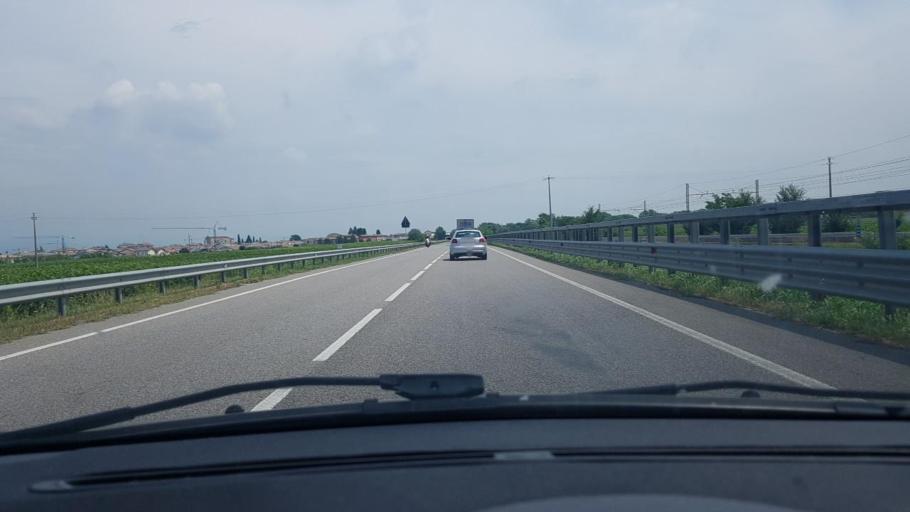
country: IT
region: Veneto
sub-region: Provincia di Verona
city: Peschiera del Garda
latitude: 45.4411
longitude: 10.6554
